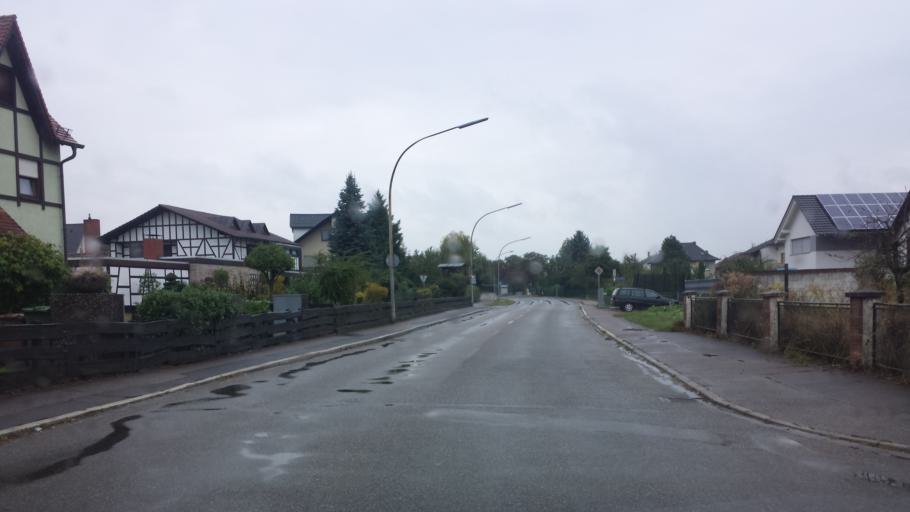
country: DE
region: Baden-Wuerttemberg
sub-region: Karlsruhe Region
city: Rauenberg
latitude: 49.2697
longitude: 8.7013
